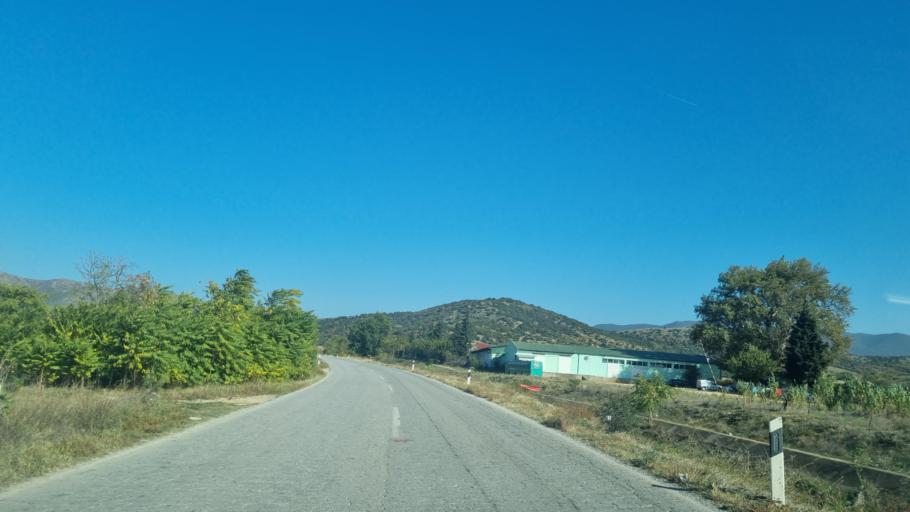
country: MK
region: Bogdanci
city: Bogdanci
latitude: 41.1966
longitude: 22.5825
